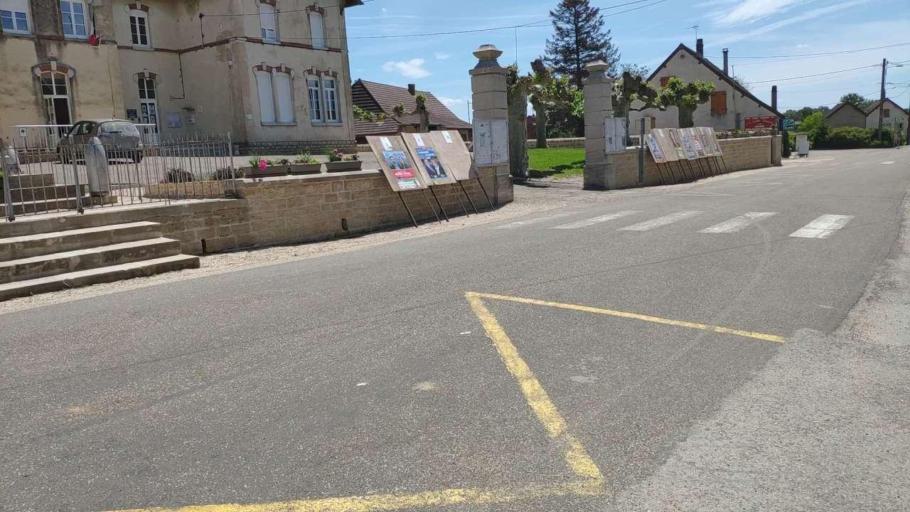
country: FR
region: Franche-Comte
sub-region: Departement du Jura
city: Bletterans
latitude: 46.8024
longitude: 5.3773
